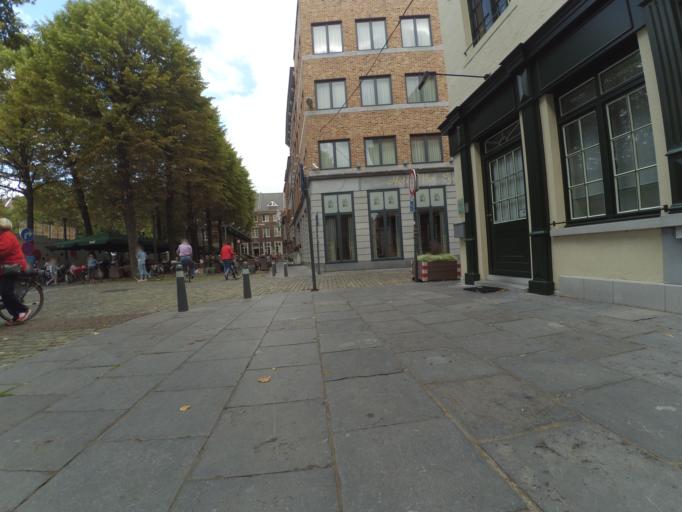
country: BE
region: Flanders
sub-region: Provincie Limburg
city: Maaseik
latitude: 51.0950
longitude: 5.7920
